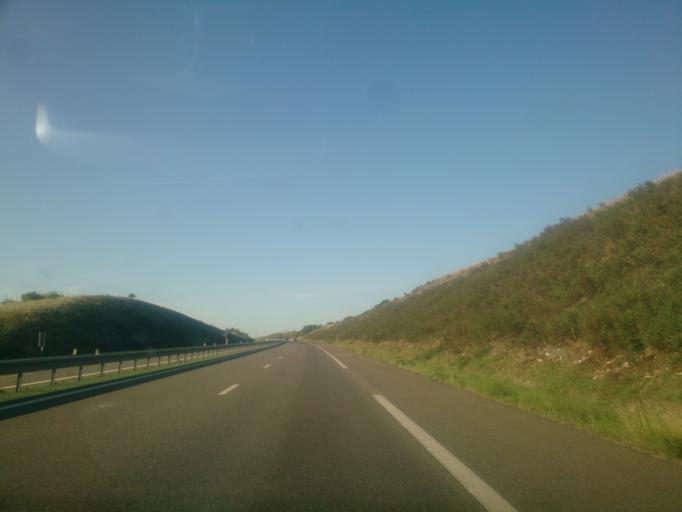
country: FR
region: Midi-Pyrenees
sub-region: Departement du Lot
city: Cahors
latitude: 44.5222
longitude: 1.5099
